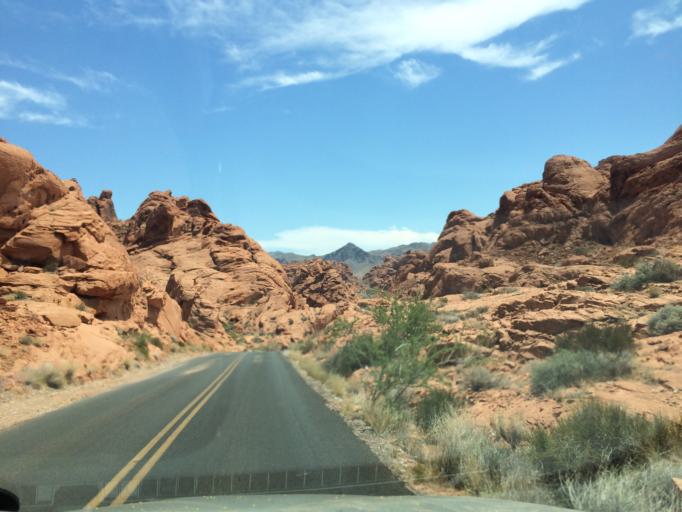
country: US
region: Nevada
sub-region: Clark County
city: Moapa Valley
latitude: 36.4500
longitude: -114.5154
